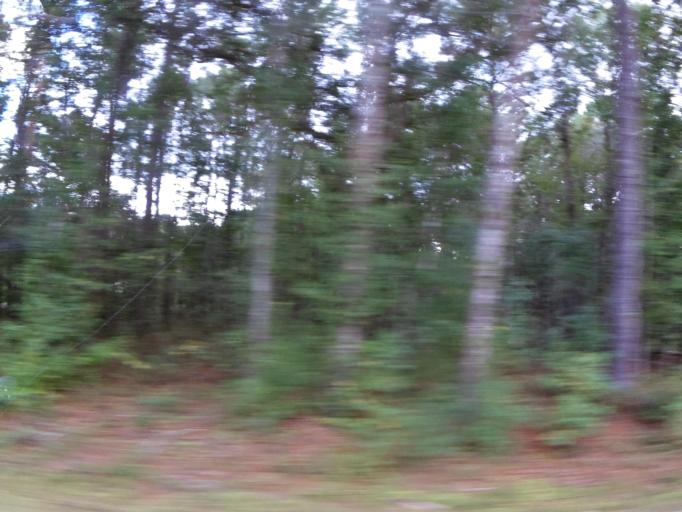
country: US
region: Georgia
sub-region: Liberty County
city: Midway
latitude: 31.8443
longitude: -81.4155
